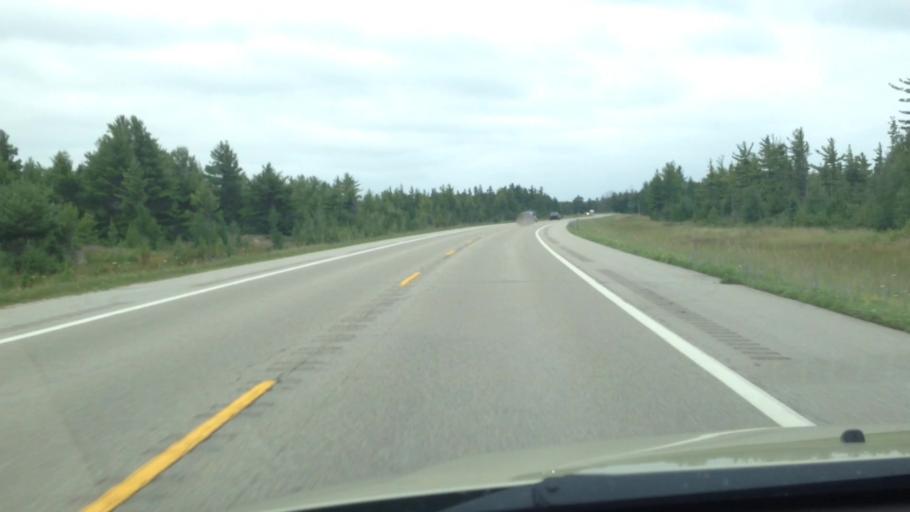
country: US
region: Michigan
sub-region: Mackinac County
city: Saint Ignace
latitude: 45.9216
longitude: -84.8772
